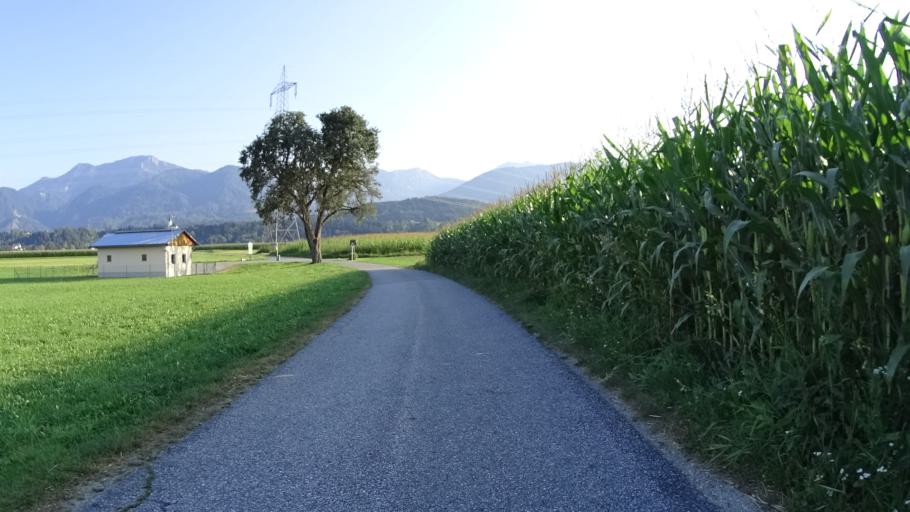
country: AT
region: Carinthia
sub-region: Politischer Bezirk Villach Land
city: Sankt Jakob
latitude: 46.5597
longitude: 14.0526
